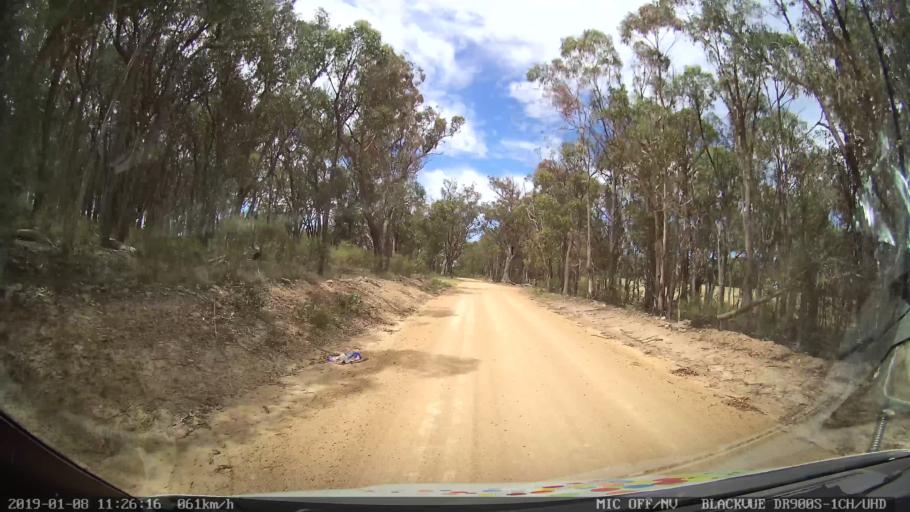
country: AU
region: New South Wales
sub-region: Guyra
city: Guyra
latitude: -30.2791
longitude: 151.5578
